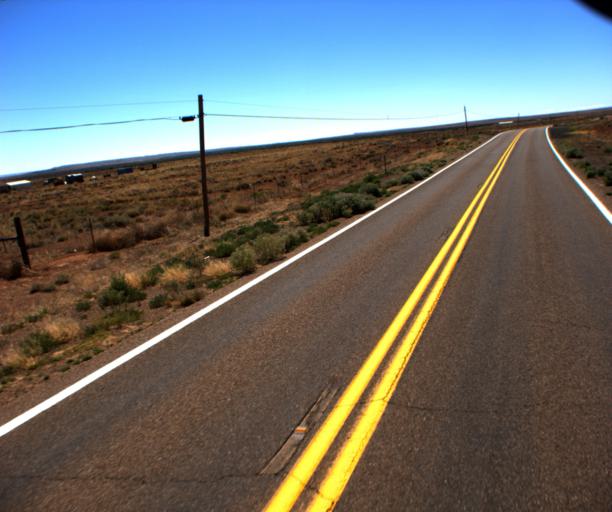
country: US
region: Arizona
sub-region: Navajo County
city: Winslow
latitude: 34.9969
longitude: -110.6742
